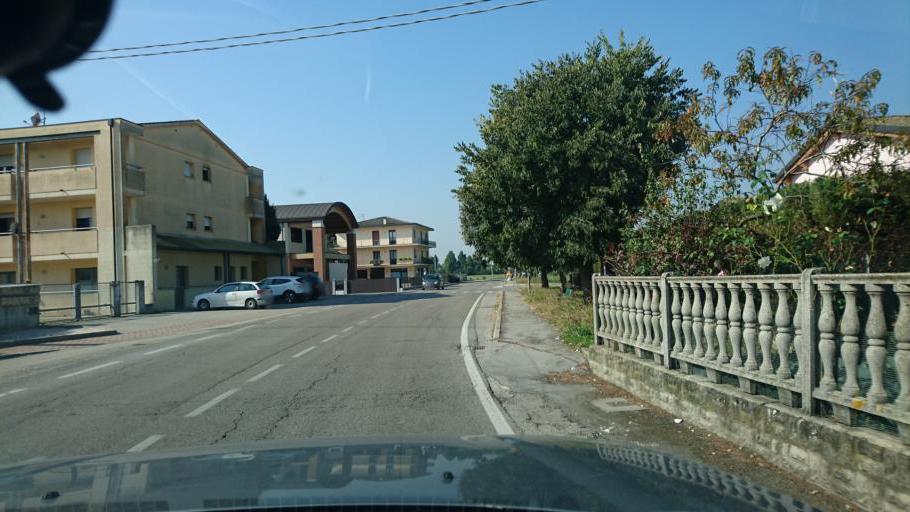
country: IT
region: Veneto
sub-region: Provincia di Padova
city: Gazzo
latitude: 45.5795
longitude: 11.6808
